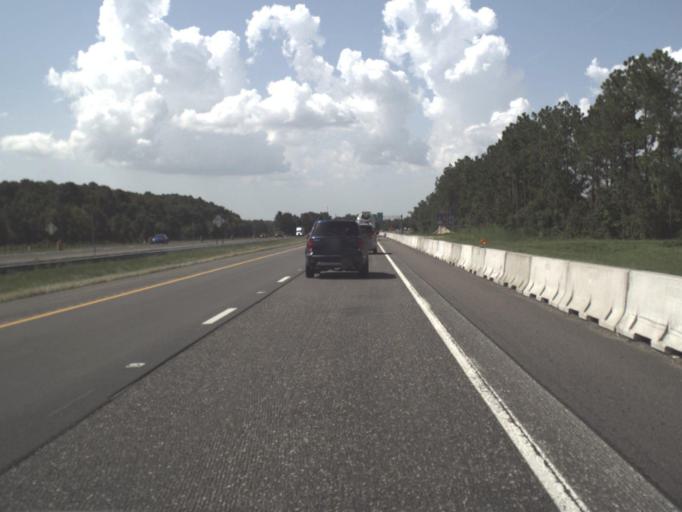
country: US
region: Florida
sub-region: Hillsborough County
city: Pebble Creek
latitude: 28.1532
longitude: -82.3894
